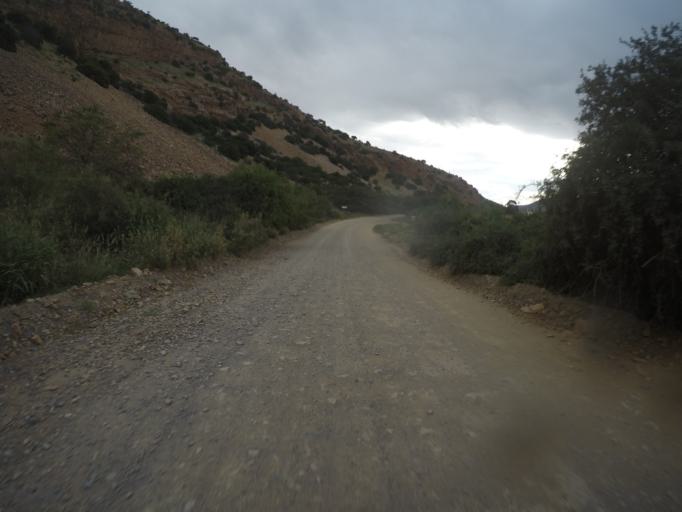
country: ZA
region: Eastern Cape
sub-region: Cacadu District Municipality
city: Willowmore
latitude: -33.5250
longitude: 23.8458
